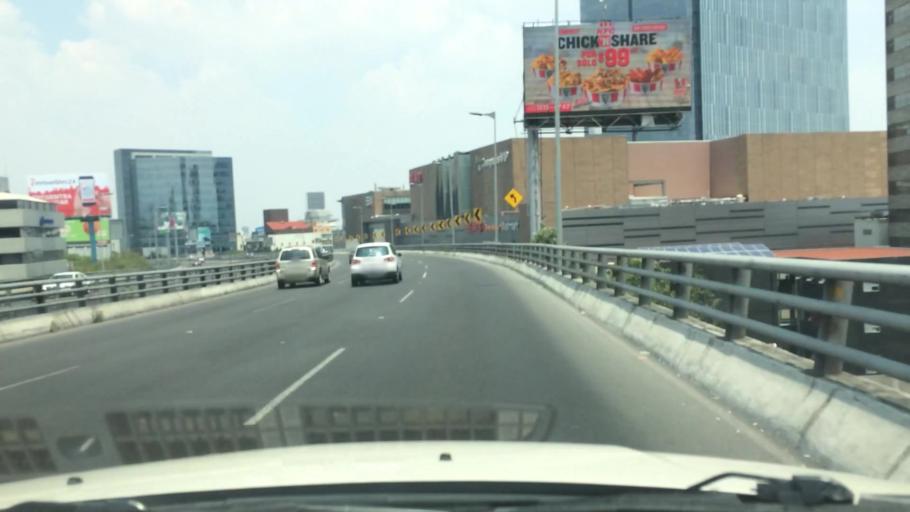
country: MX
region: Mexico City
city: Alvaro Obregon
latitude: 19.3599
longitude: -99.1926
